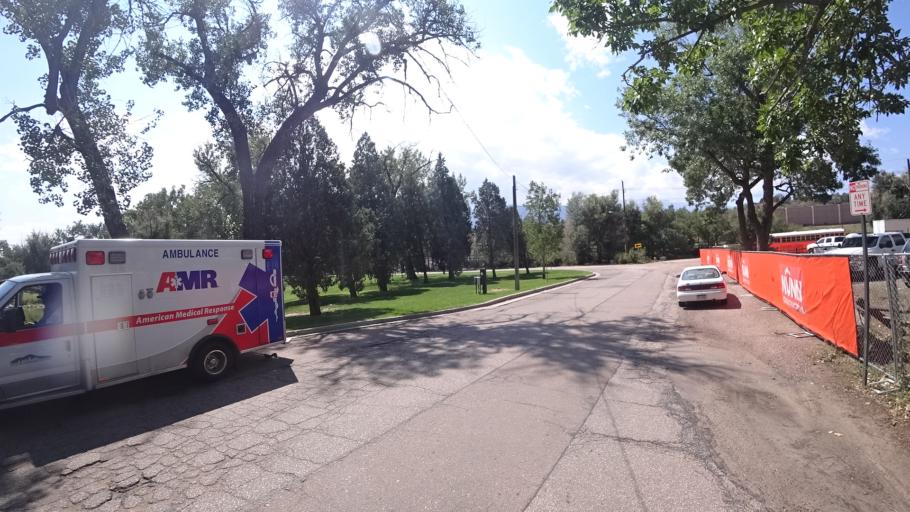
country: US
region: Colorado
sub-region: El Paso County
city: Colorado Springs
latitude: 38.8495
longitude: -104.8298
